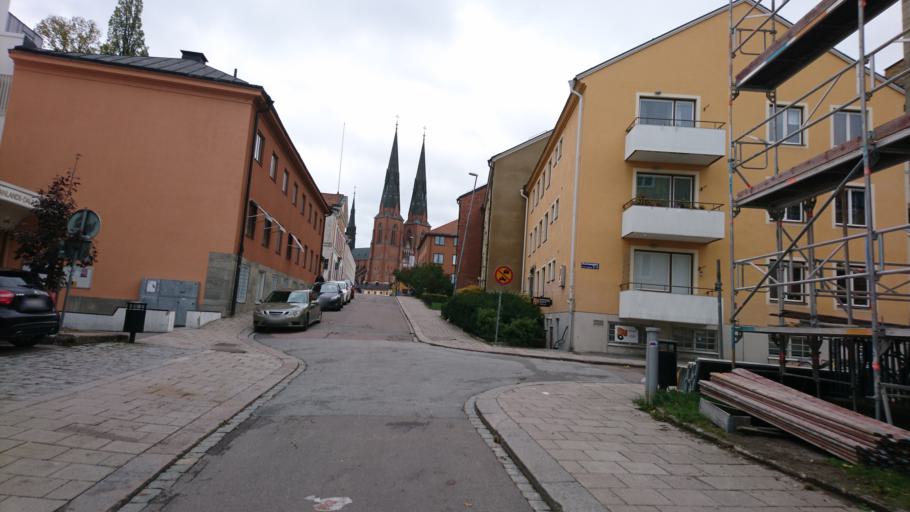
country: SE
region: Uppsala
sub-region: Uppsala Kommun
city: Uppsala
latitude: 59.8601
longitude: 17.6283
